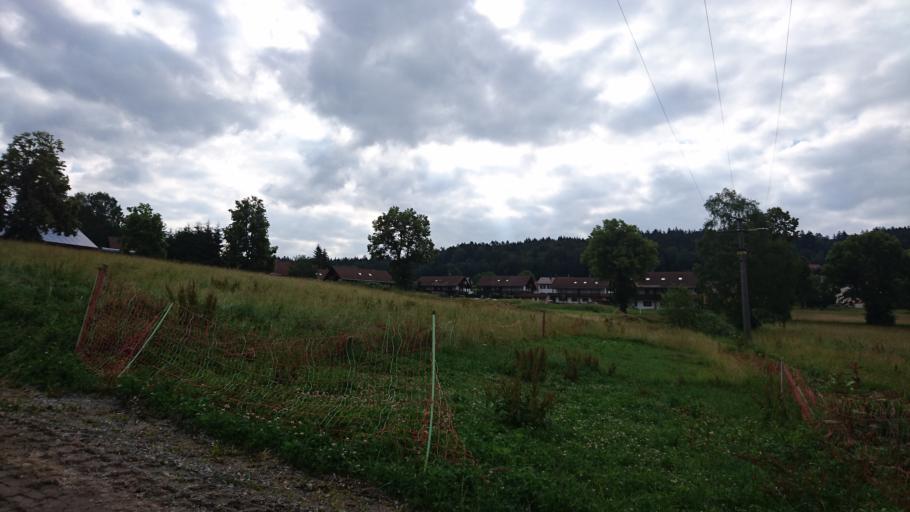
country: DE
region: Bavaria
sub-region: Lower Bavaria
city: Neuschonau
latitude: 48.8819
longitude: 13.4756
